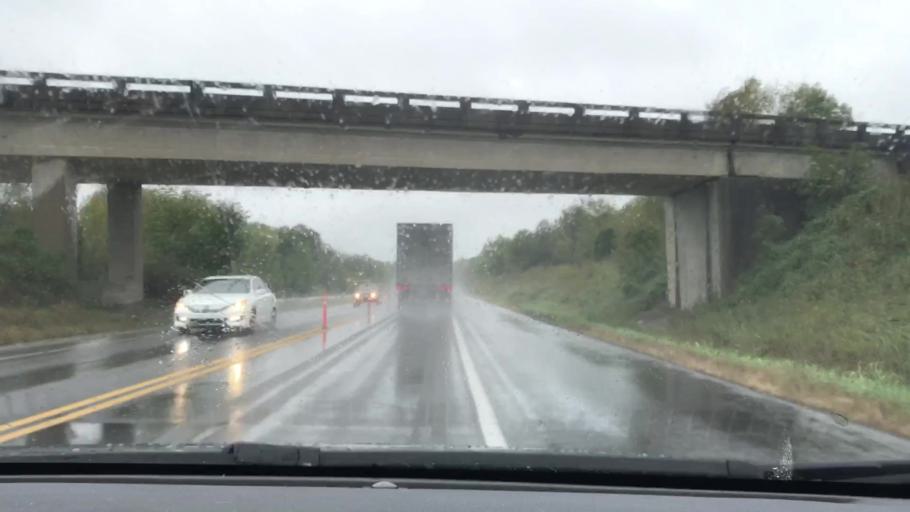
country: US
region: Kentucky
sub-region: Christian County
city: Hopkinsville
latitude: 37.0088
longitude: -87.4591
